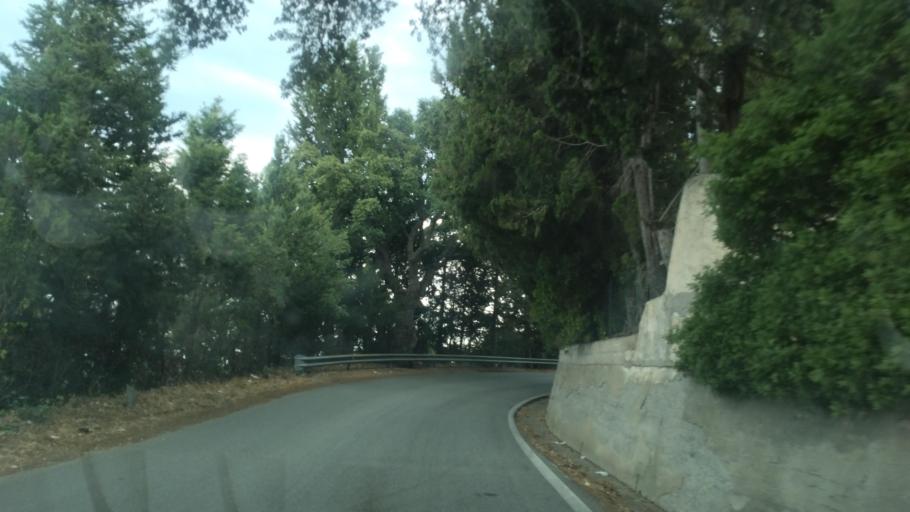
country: IT
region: Calabria
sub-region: Provincia di Catanzaro
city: Squillace Lido
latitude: 38.7589
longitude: 16.5671
